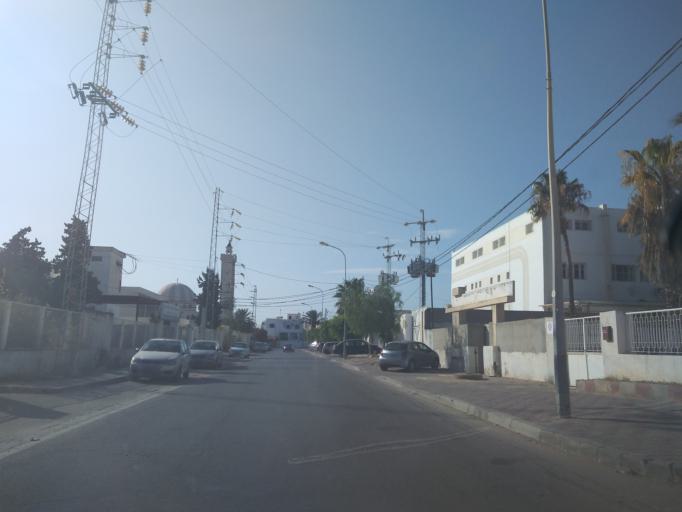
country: TN
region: Safaqis
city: Al Qarmadah
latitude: 34.7491
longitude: 10.7724
